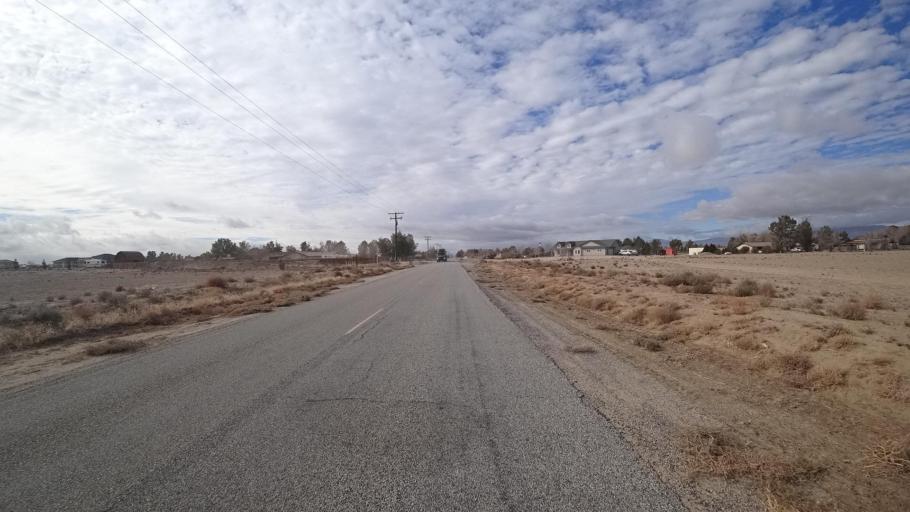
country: US
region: California
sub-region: Kern County
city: Rosamond
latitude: 34.8201
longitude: -118.2588
